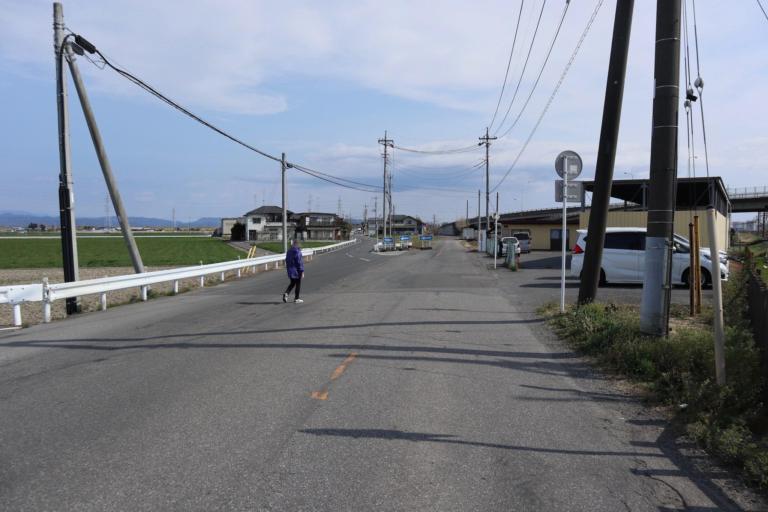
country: JP
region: Gunma
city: Tatebayashi
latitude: 36.2638
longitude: 139.5426
